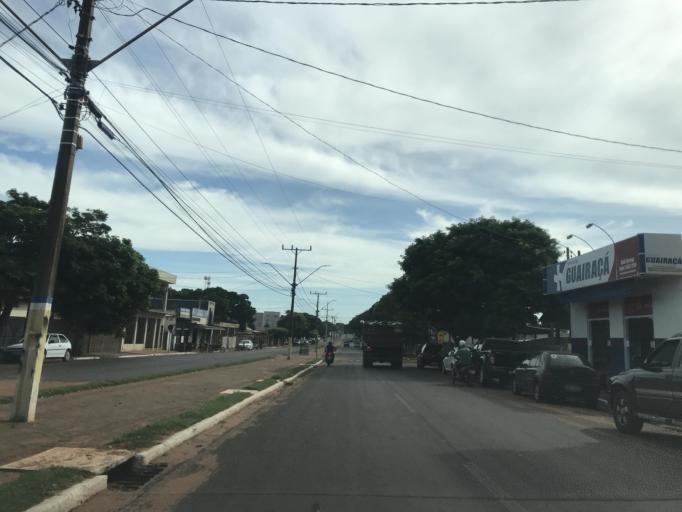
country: BR
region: Parana
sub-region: Paranavai
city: Nova Aurora
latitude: -22.9400
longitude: -52.6897
